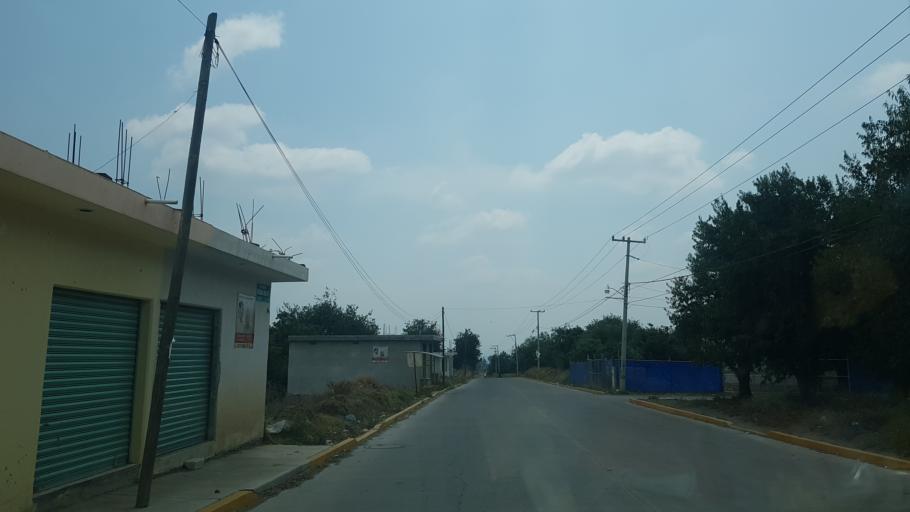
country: MX
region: Puebla
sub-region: Huejotzingo
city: San Juan Pancoac
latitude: 19.1388
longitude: -98.4388
